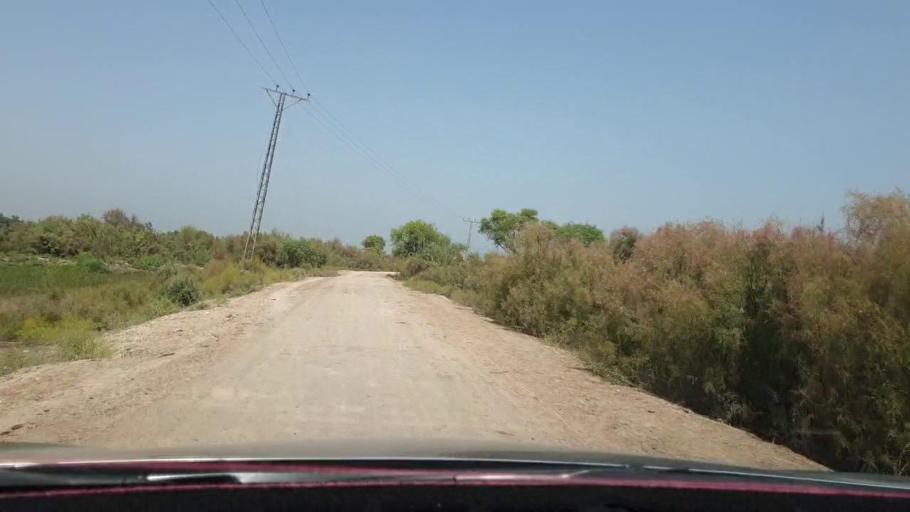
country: PK
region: Sindh
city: Warah
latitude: 27.4034
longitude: 67.6909
